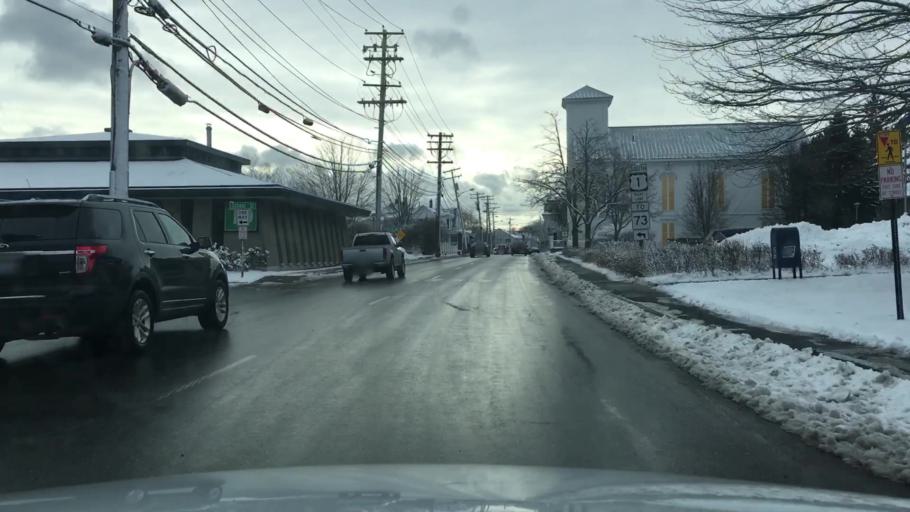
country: US
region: Maine
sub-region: Knox County
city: Rockland
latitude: 44.1042
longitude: -69.1112
